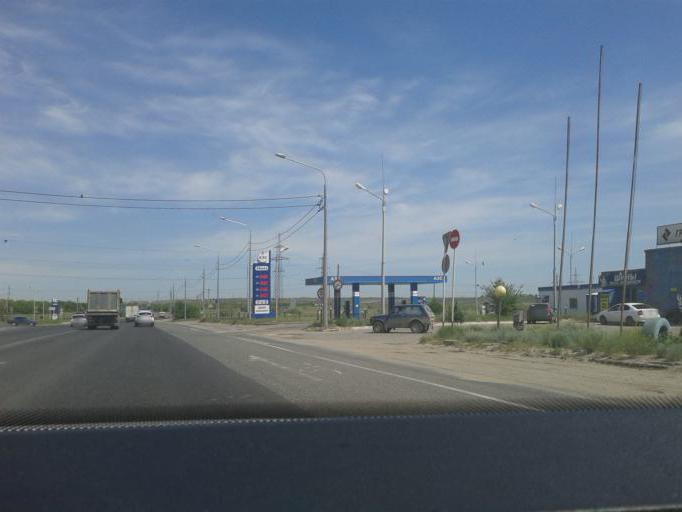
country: RU
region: Volgograd
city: Vodstroy
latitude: 48.8210
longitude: 44.5257
